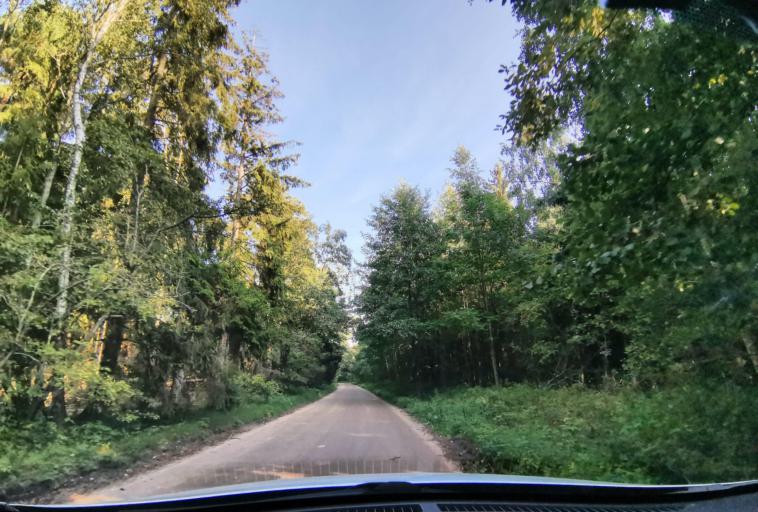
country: LT
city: Nida
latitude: 55.1602
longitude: 20.8344
